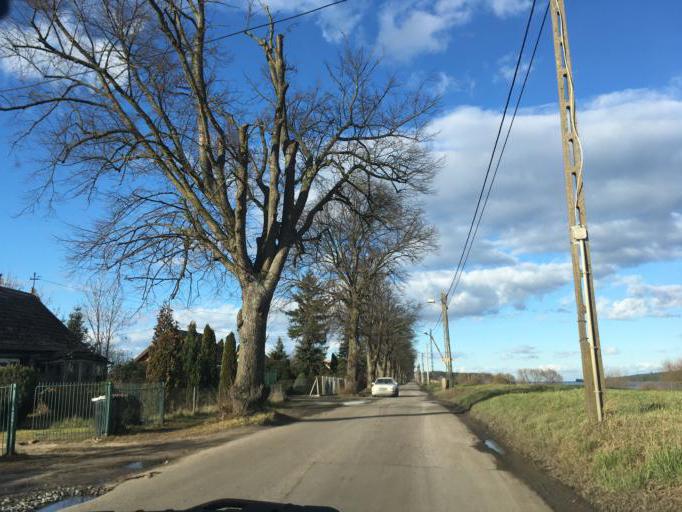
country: PL
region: Pomeranian Voivodeship
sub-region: Powiat nowodworski
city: Ostaszewo
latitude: 54.3227
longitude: 18.9319
